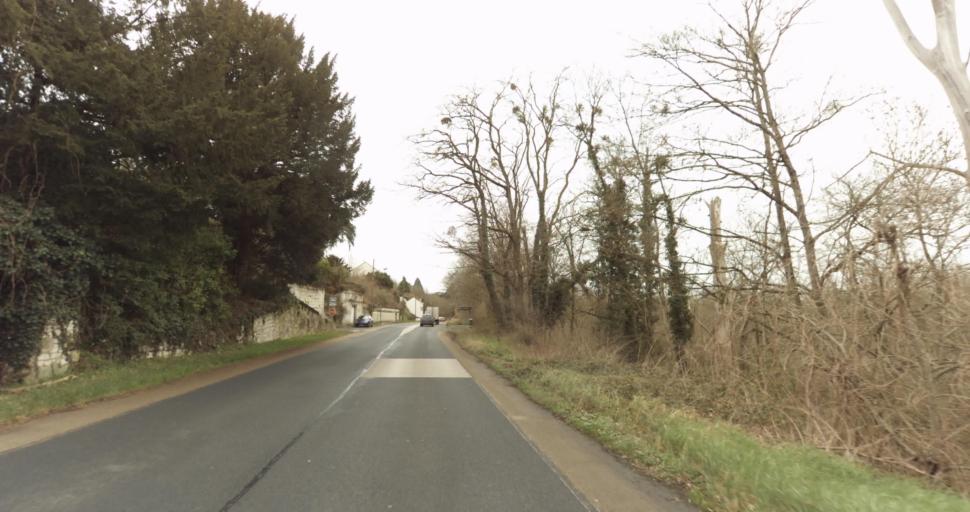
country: FR
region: Pays de la Loire
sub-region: Departement de Maine-et-Loire
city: Villebernier
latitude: 47.2464
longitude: -0.0405
